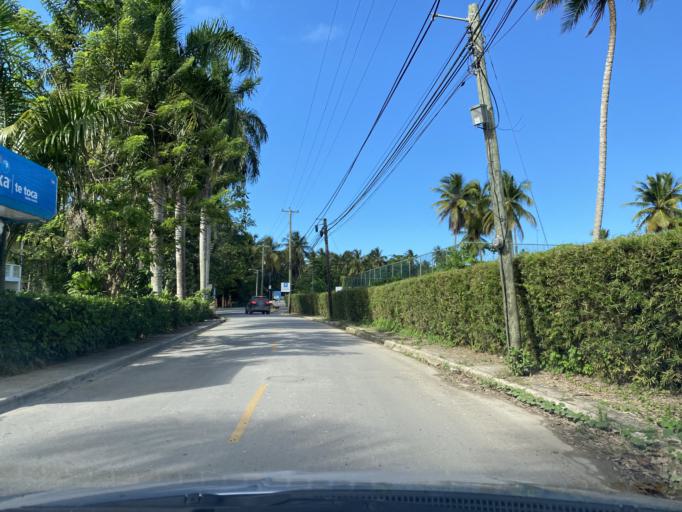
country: DO
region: Samana
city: Las Terrenas
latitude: 19.3098
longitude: -69.5642
